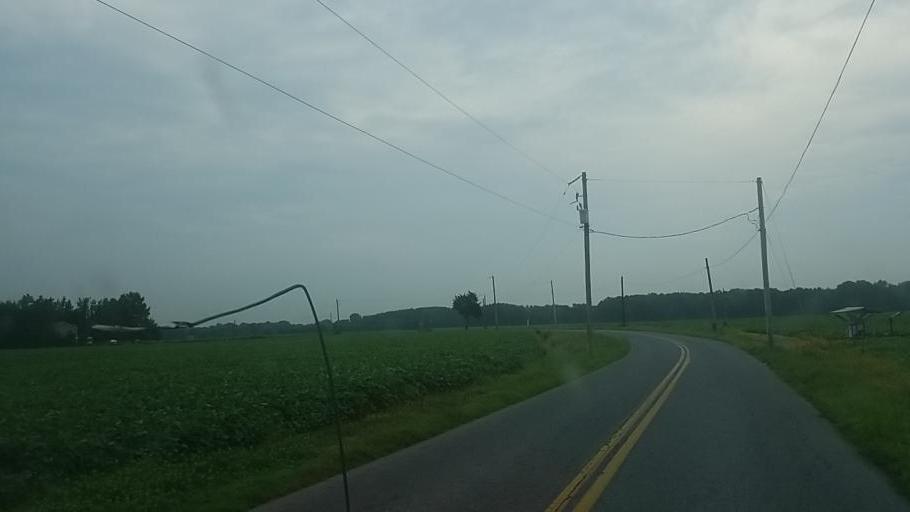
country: US
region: Delaware
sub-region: Sussex County
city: Selbyville
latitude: 38.4484
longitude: -75.2202
